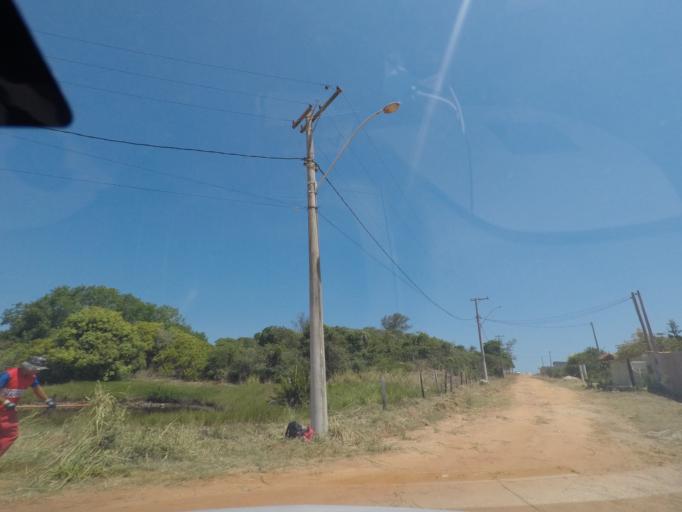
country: BR
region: Rio de Janeiro
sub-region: Marica
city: Marica
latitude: -22.9720
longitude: -42.9289
